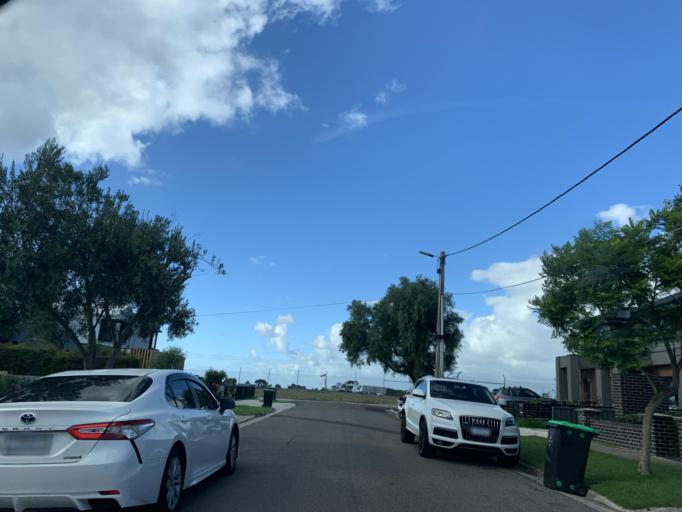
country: AU
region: Victoria
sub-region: Moreland
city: Oak Park
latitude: -37.7285
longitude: 144.9138
